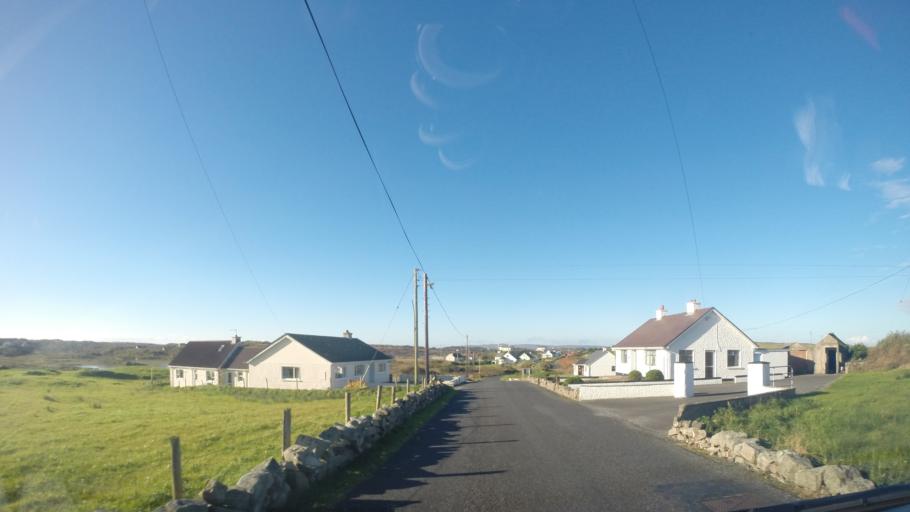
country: IE
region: Ulster
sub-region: County Donegal
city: Dungloe
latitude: 55.0325
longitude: -8.3624
